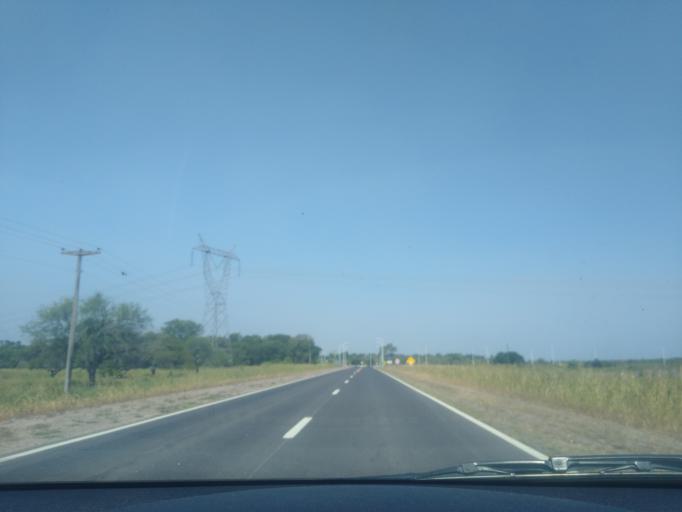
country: AR
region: Chaco
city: Fontana
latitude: -27.5768
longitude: -59.1614
